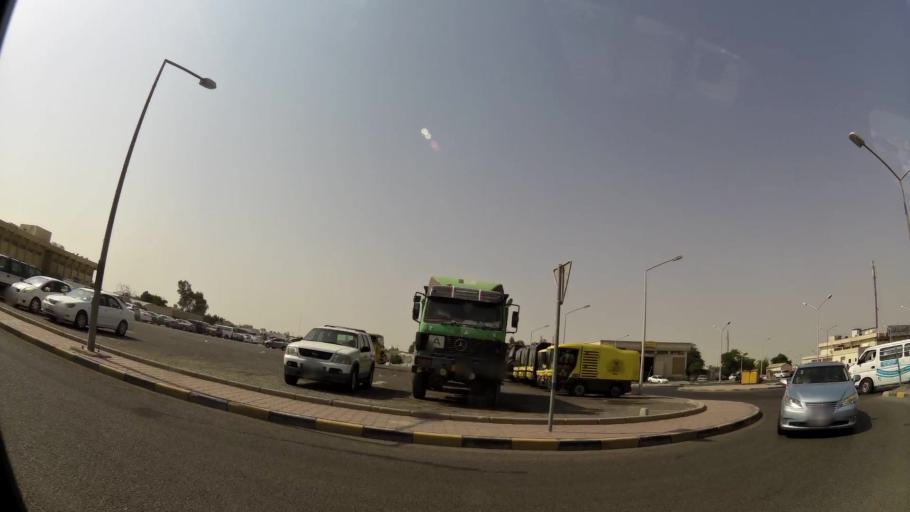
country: KW
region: Muhafazat al Jahra'
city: Al Jahra'
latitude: 29.3264
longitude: 47.6808
